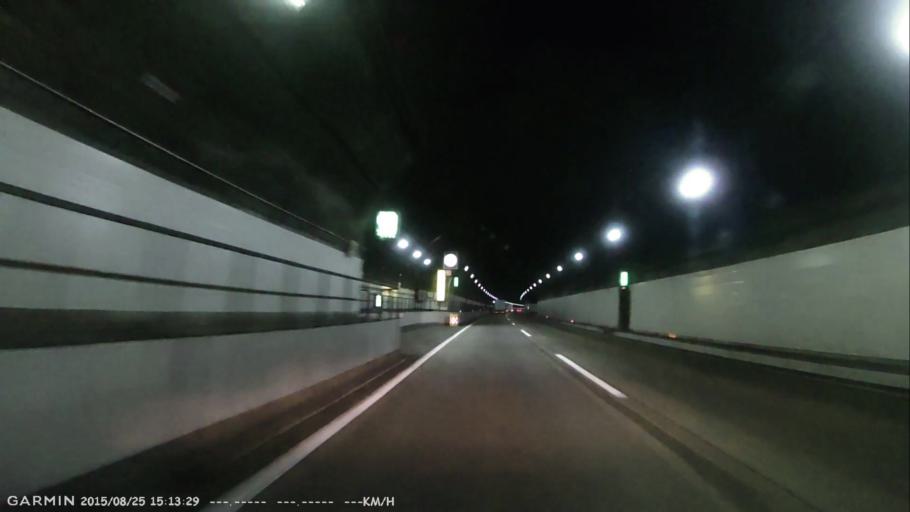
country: JP
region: Fukushima
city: Inawashiro
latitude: 37.4984
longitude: 140.2317
